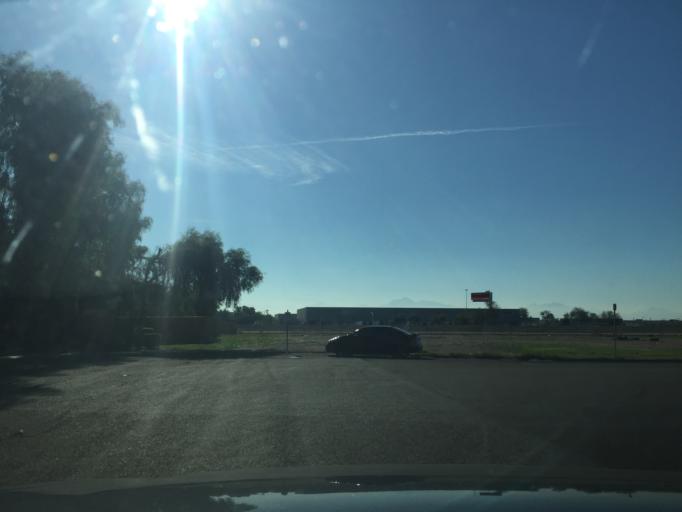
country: US
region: Arizona
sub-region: Maricopa County
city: Tolleson
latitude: 33.4645
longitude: -112.2164
